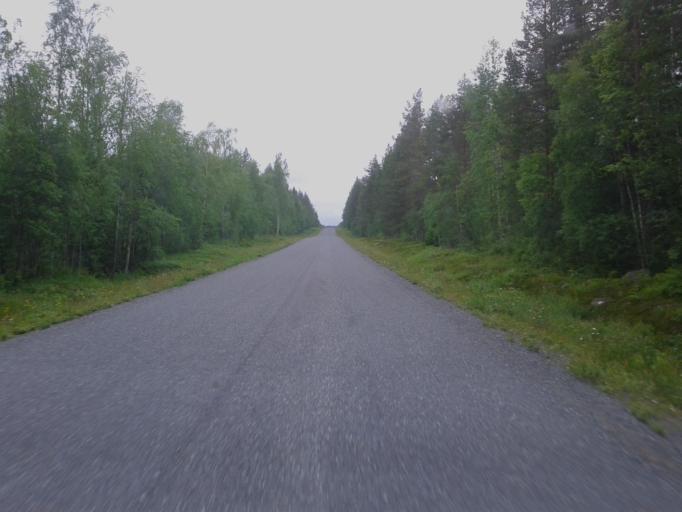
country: SE
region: Vaesterbotten
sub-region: Skelleftea Kommun
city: Storvik
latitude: 65.0035
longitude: 20.7469
